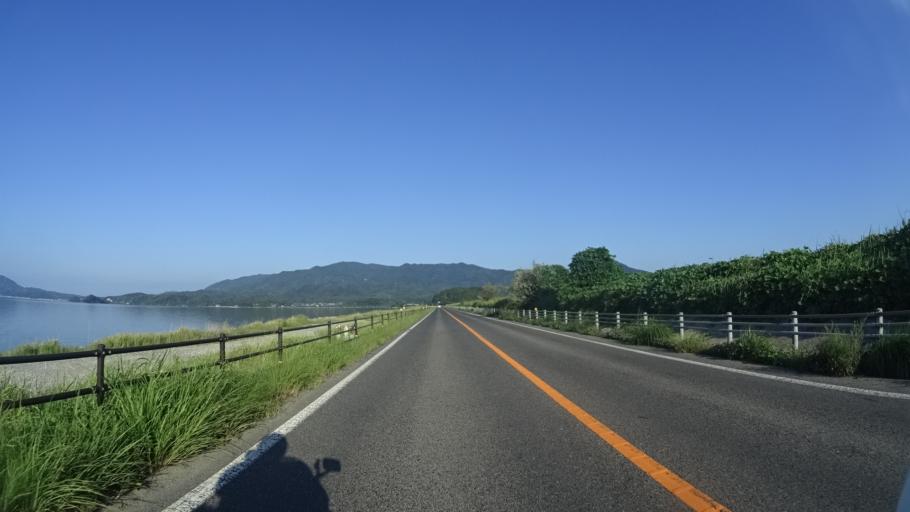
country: JP
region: Shimane
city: Sakaiminato
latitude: 35.5278
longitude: 133.1716
